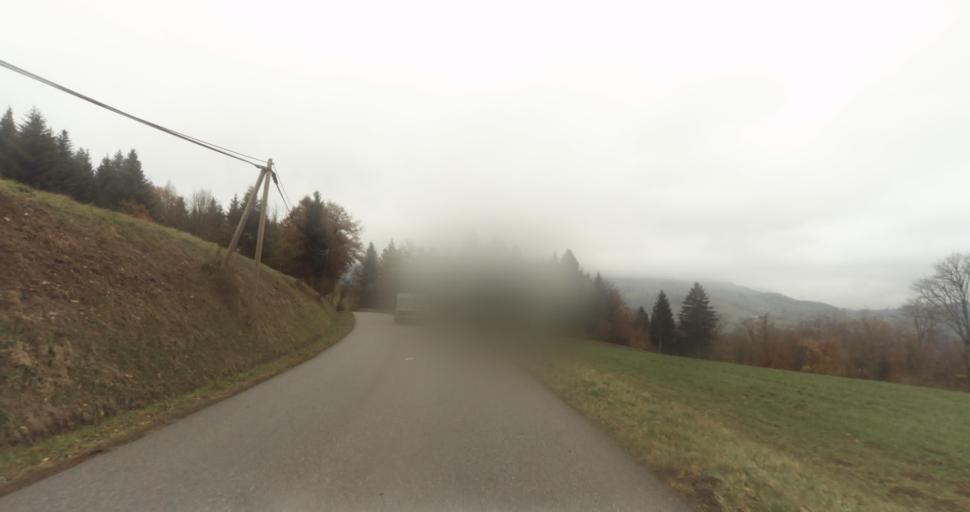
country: FR
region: Rhone-Alpes
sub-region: Departement de la Haute-Savoie
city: Thorens-Glieres
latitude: 46.0078
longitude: 6.2383
